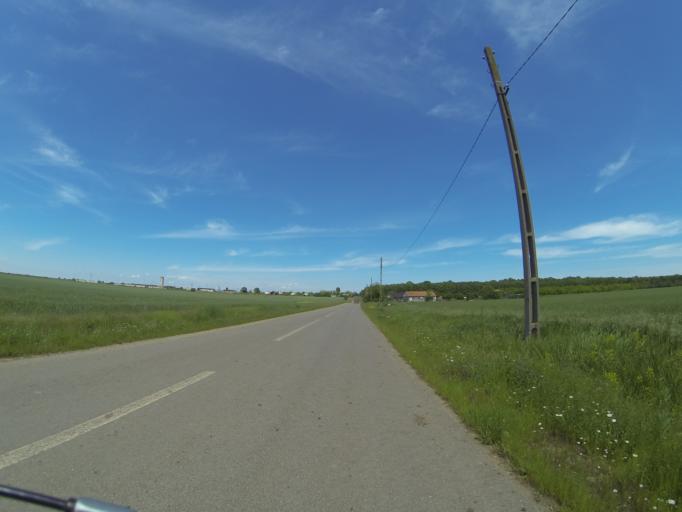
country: RO
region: Dolj
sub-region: Comuna Teslui
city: Teslui
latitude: 44.1659
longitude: 24.1602
